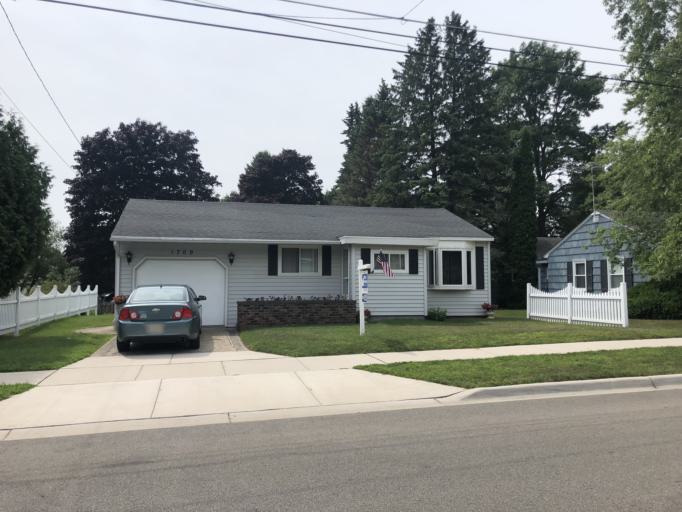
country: US
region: Michigan
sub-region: Menominee County
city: Menominee
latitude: 45.1262
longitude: -87.6232
